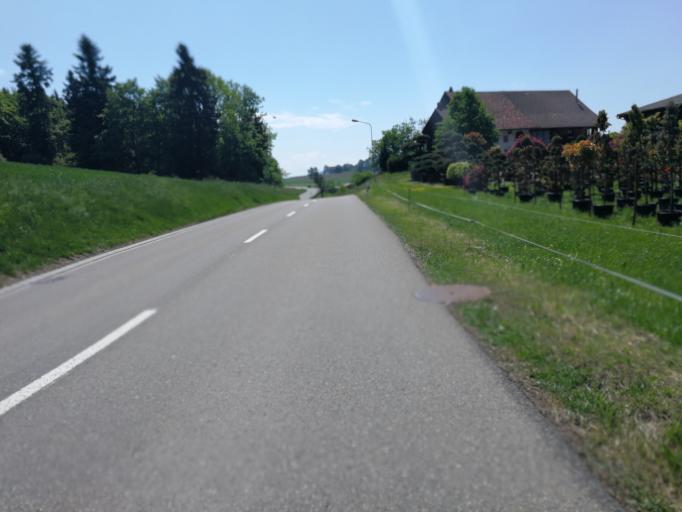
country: CH
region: Zurich
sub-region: Bezirk Uster
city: Aesch
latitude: 47.3129
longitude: 8.6402
